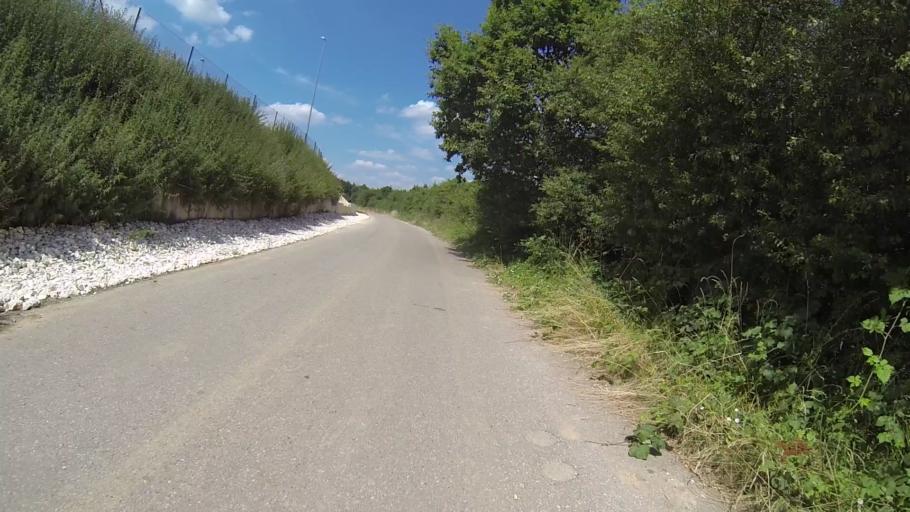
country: DE
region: Baden-Wuerttemberg
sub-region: Regierungsbezirk Stuttgart
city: Giengen an der Brenz
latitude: 48.6178
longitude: 10.2108
